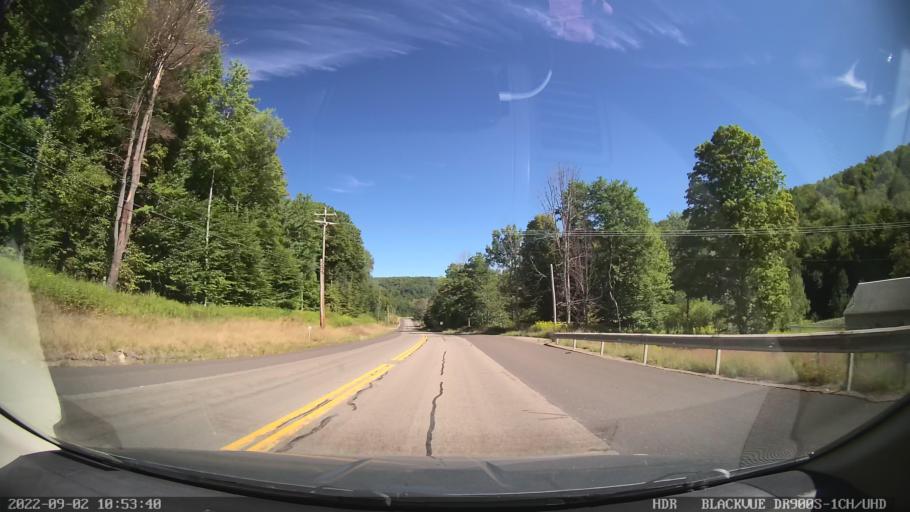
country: US
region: Pennsylvania
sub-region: Tioga County
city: Blossburg
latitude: 41.6491
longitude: -77.0959
